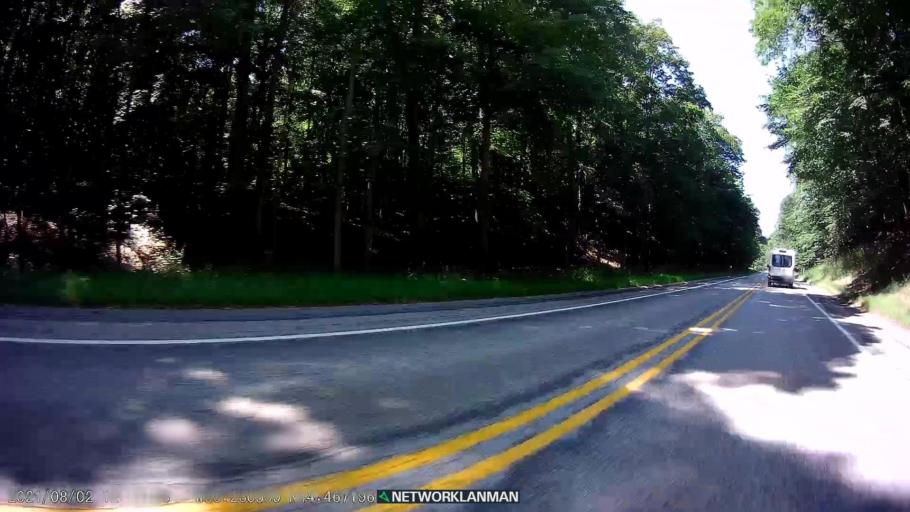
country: US
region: Michigan
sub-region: Benzie County
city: Frankfort
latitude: 44.4672
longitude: -86.2308
